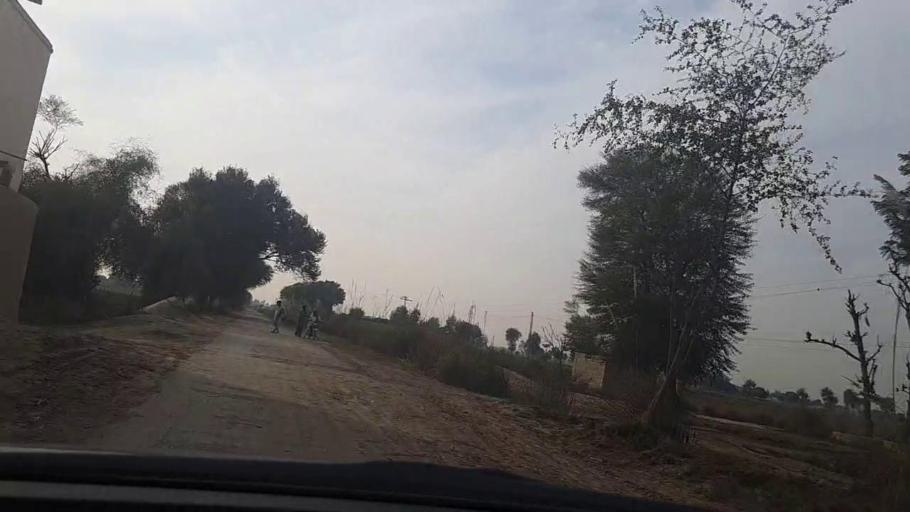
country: PK
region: Sindh
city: Daulatpur
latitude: 26.3340
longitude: 68.0599
